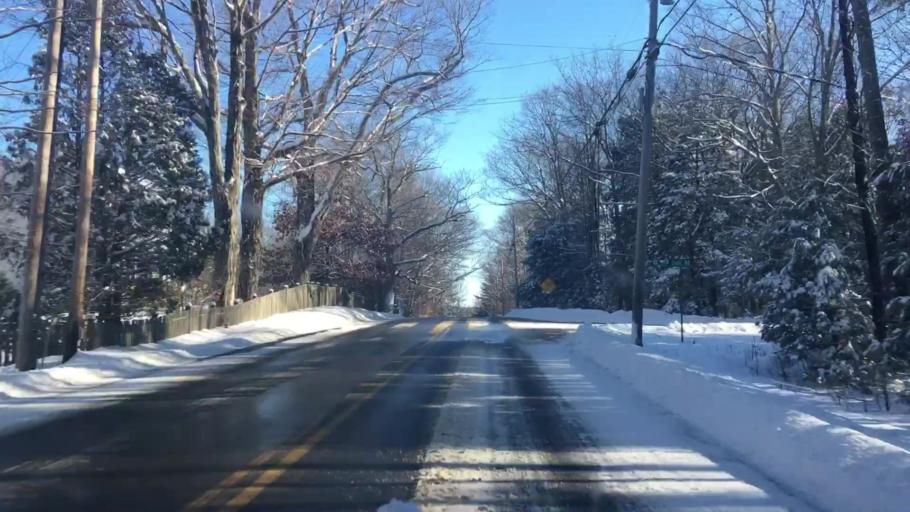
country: US
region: Maine
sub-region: Androscoggin County
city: Lisbon Falls
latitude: 43.9389
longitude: -70.0672
